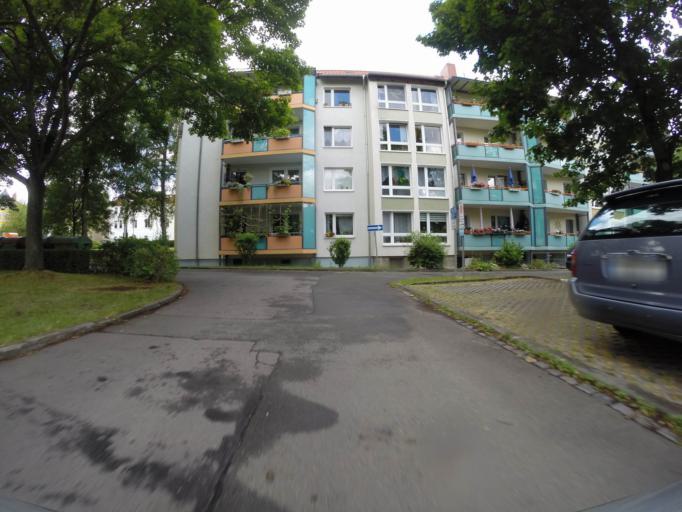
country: DE
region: Thuringia
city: Jena
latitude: 50.9454
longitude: 11.5980
